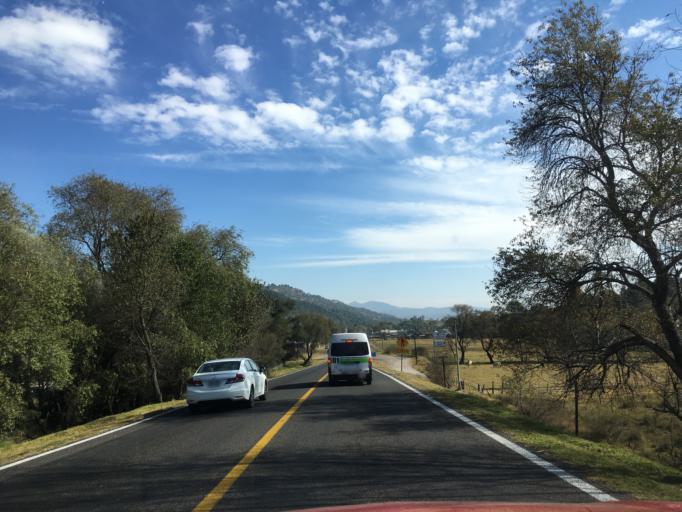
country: MX
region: Michoacan
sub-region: Hidalgo
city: San Lucas Huarirapeo (La Mesa de San Lucas)
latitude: 19.6688
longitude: -100.6706
